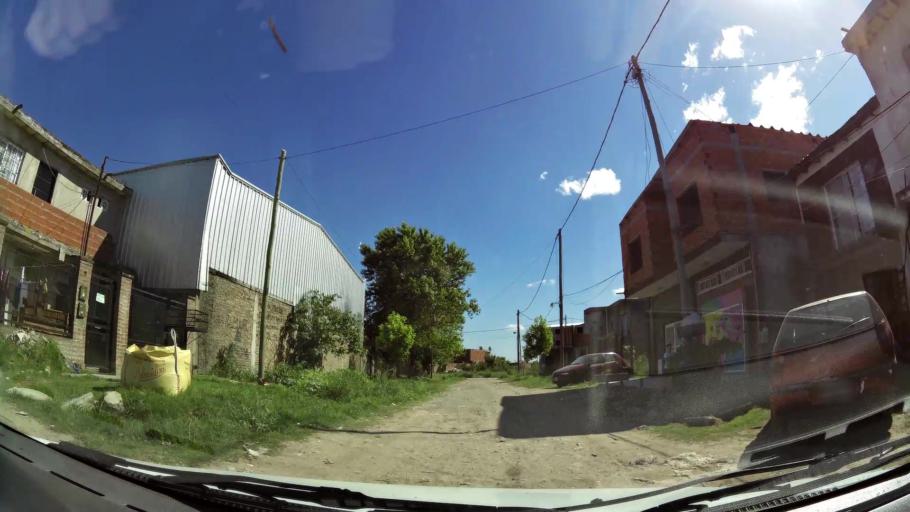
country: AR
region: Buenos Aires
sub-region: Partido de General San Martin
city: General San Martin
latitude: -34.5167
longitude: -58.5849
